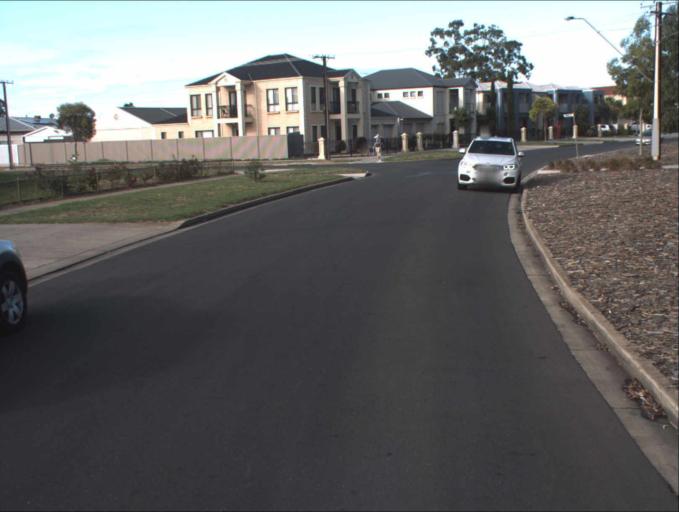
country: AU
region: South Australia
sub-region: Charles Sturt
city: Woodville North
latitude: -34.8597
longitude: 138.5543
